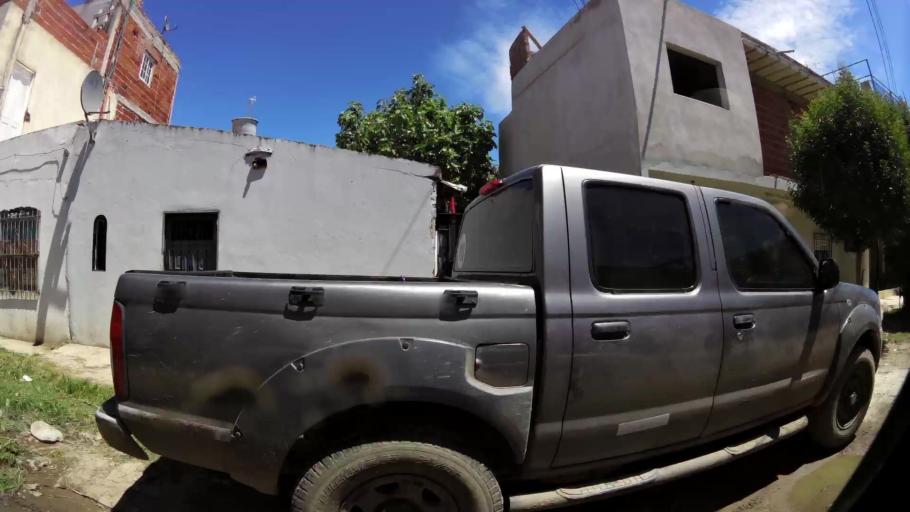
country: AR
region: Buenos Aires
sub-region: Partido de Quilmes
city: Quilmes
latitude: -34.7213
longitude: -58.3228
